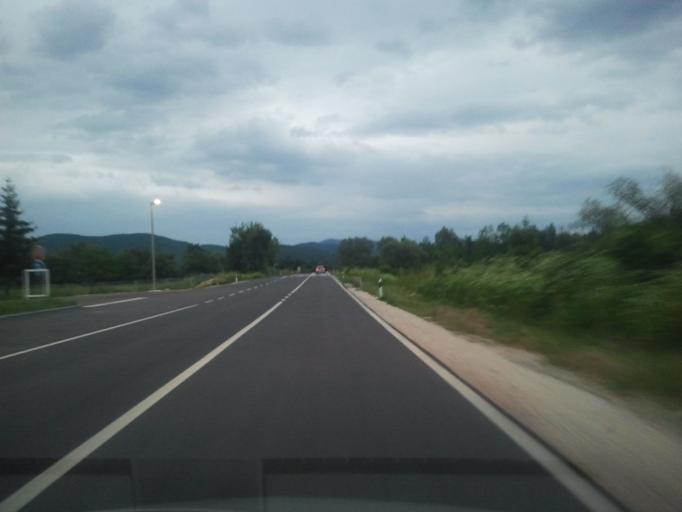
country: HR
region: Zadarska
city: Gracac
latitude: 44.2956
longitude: 15.8474
